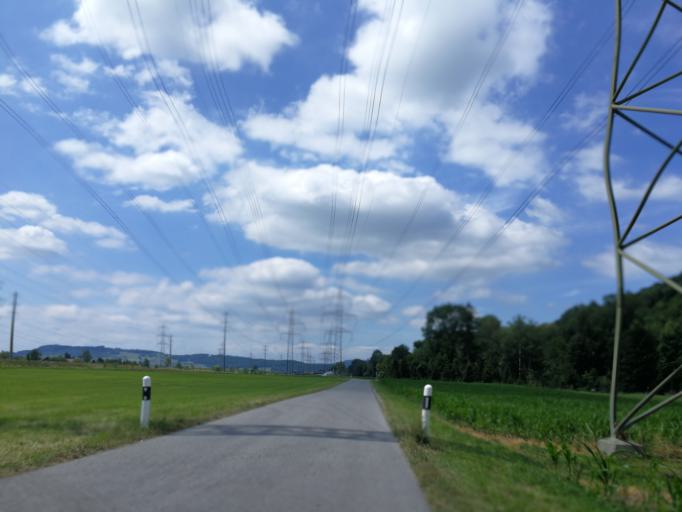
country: CH
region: Saint Gallen
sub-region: Wahlkreis See-Gaster
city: Benken
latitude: 47.1740
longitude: 9.0078
